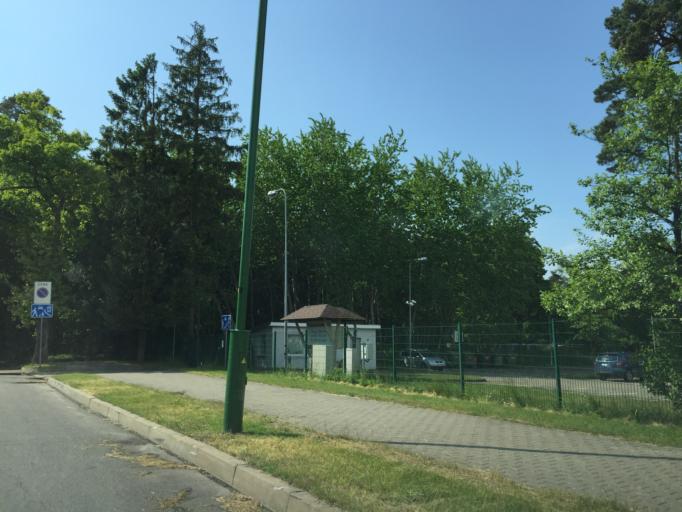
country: LT
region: Klaipedos apskritis
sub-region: Klaipeda
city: Klaipeda
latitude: 55.7697
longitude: 21.0894
